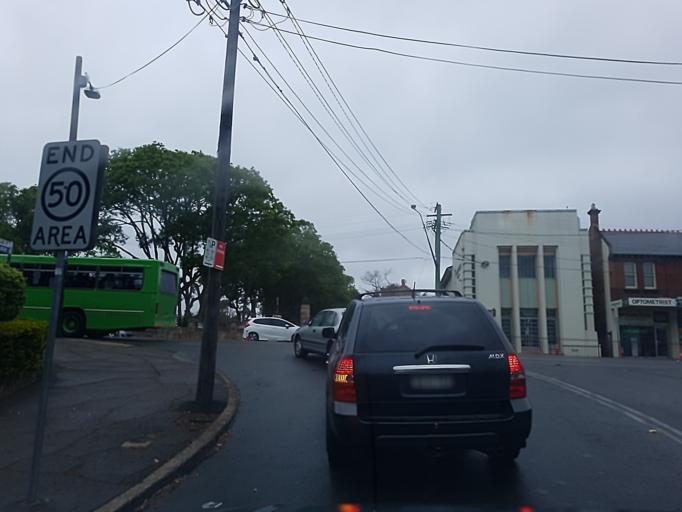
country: AU
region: New South Wales
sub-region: City of Sydney
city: Pymble
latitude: -33.7332
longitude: 151.1284
